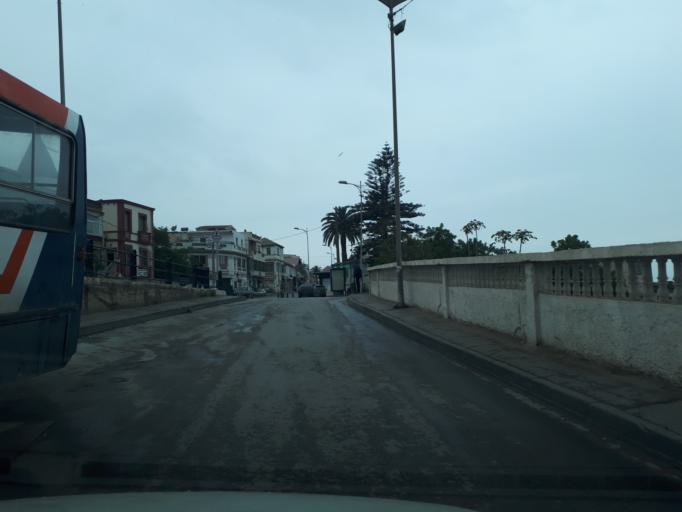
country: DZ
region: Alger
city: Algiers
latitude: 36.8166
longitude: 3.0152
